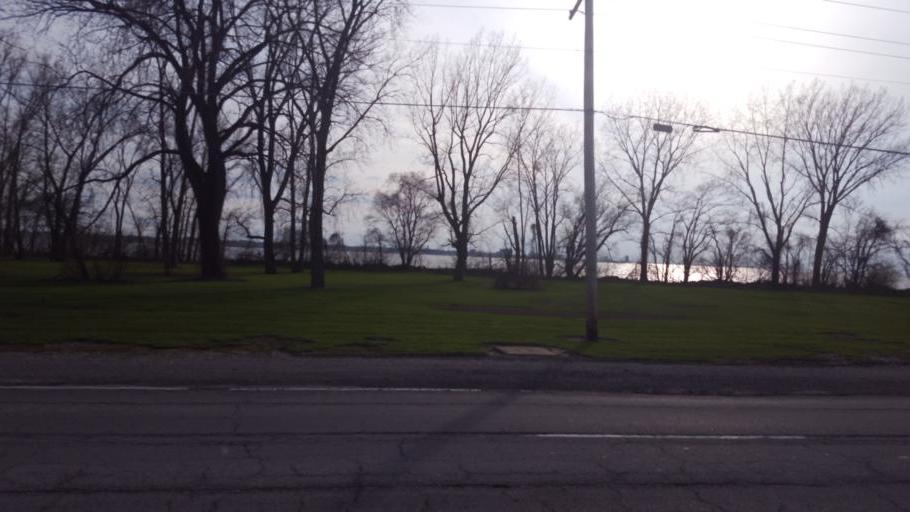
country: US
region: Ohio
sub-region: Erie County
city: Sandusky
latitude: 41.4662
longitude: -82.6736
